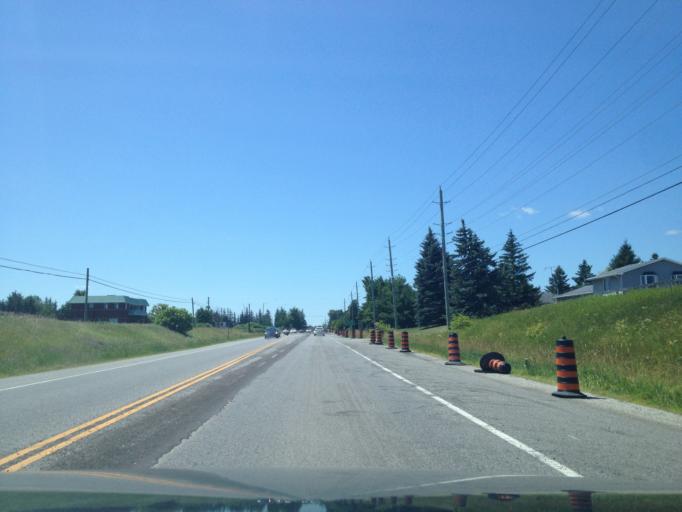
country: CA
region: Ontario
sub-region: Halton
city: Milton
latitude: 43.6489
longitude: -80.0156
